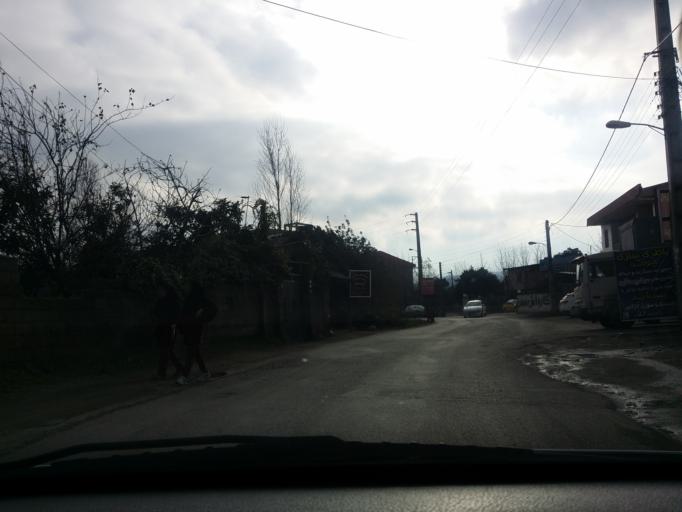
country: IR
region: Mazandaran
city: Chalus
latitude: 36.6597
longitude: 51.4016
